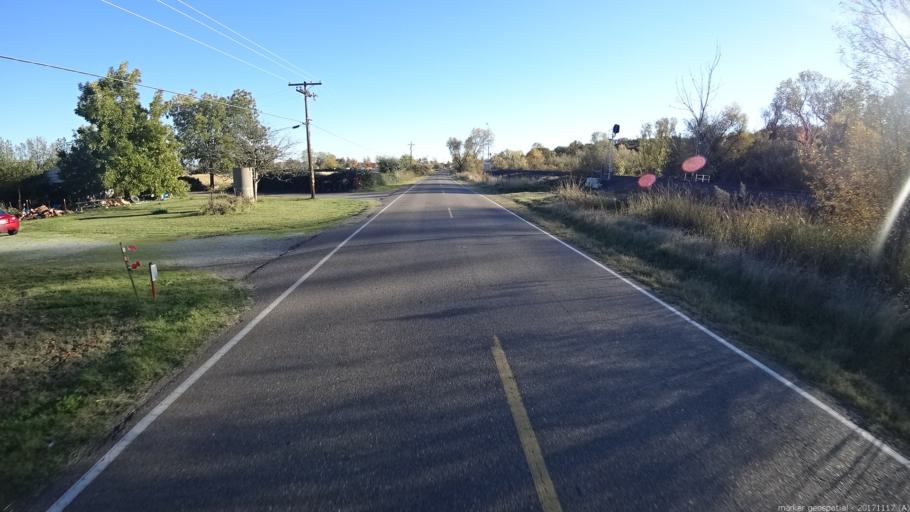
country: US
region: California
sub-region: Shasta County
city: Cottonwood
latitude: 40.4108
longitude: -122.2463
